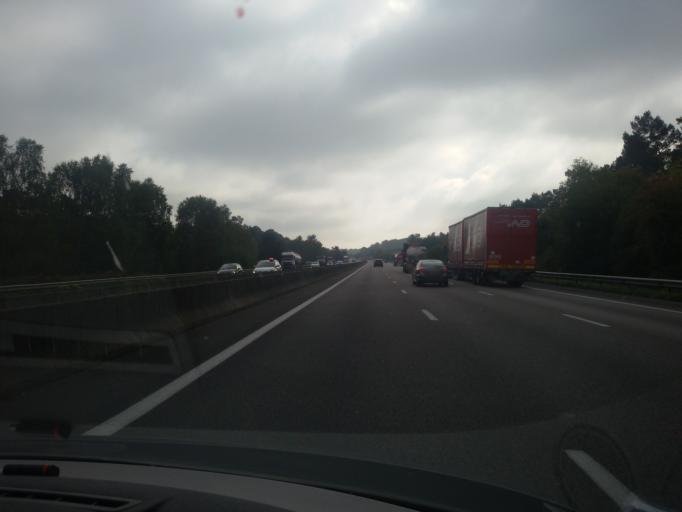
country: FR
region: Haute-Normandie
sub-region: Departement de l'Eure
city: Criquebeuf-sur-Seine
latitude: 49.2861
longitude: 1.1255
